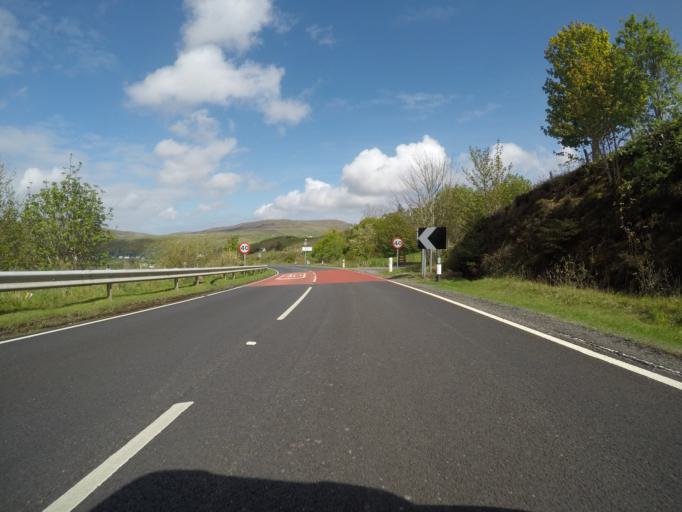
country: GB
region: Scotland
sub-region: Highland
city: Portree
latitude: 57.5809
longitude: -6.3607
